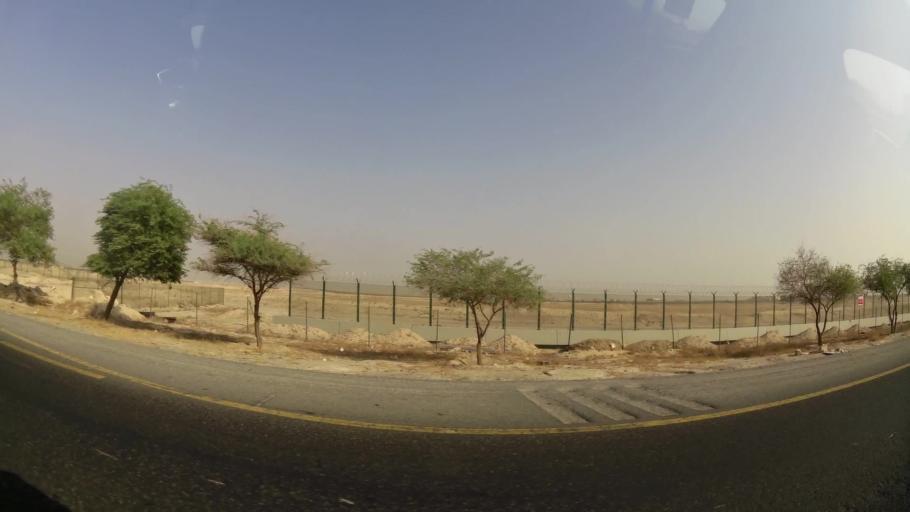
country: KW
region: Al Farwaniyah
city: Janub as Surrah
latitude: 29.1833
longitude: 47.9522
